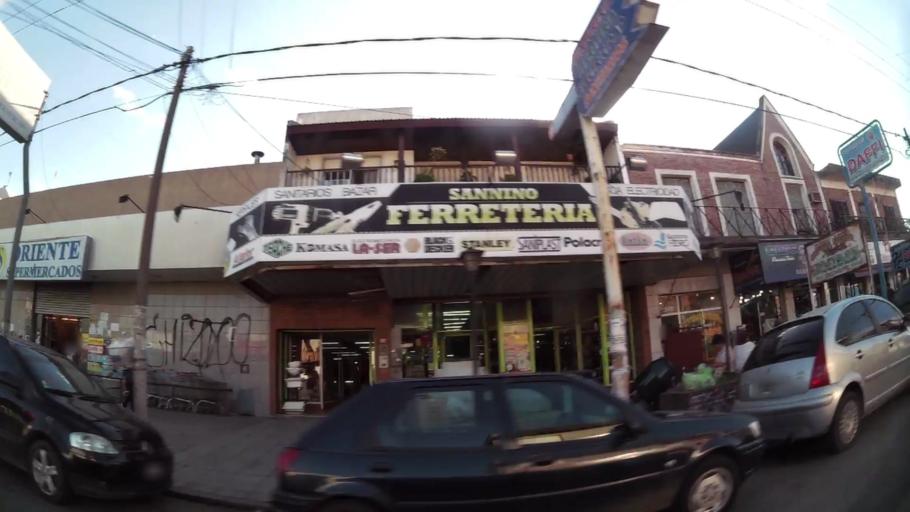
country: AR
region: Buenos Aires
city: Santa Catalina - Dique Lujan
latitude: -34.4857
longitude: -58.7271
